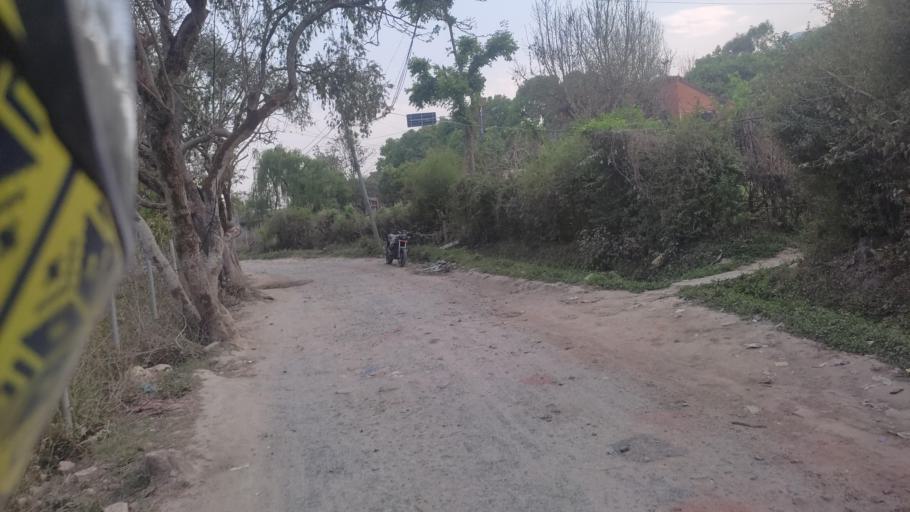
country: NP
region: Central Region
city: Kirtipur
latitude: 27.6839
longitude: 85.2837
